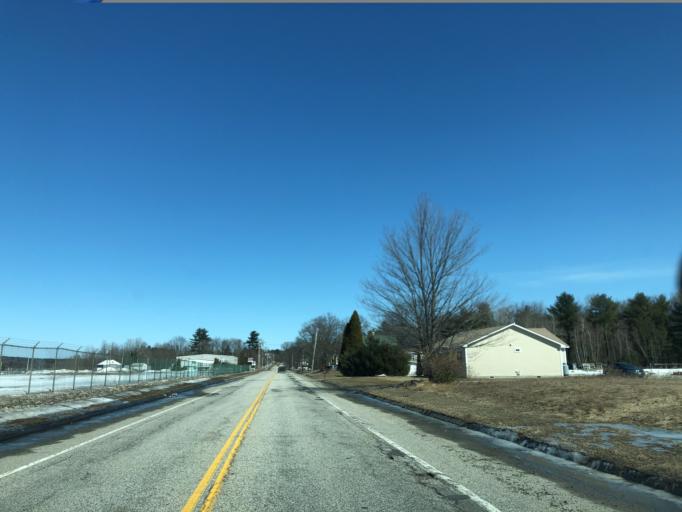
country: US
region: Maine
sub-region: Androscoggin County
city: Minot
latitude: 44.0439
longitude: -70.2781
